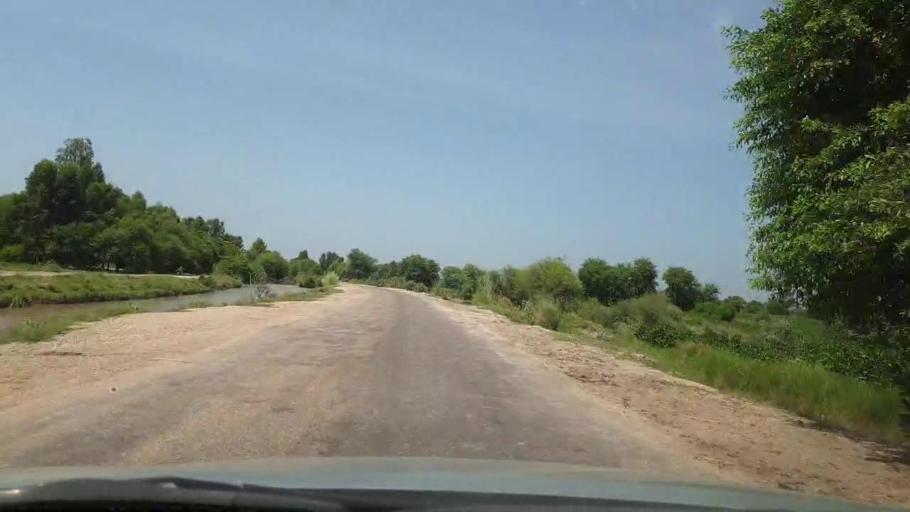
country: PK
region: Sindh
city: Pano Aqil
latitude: 27.6878
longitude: 69.1107
